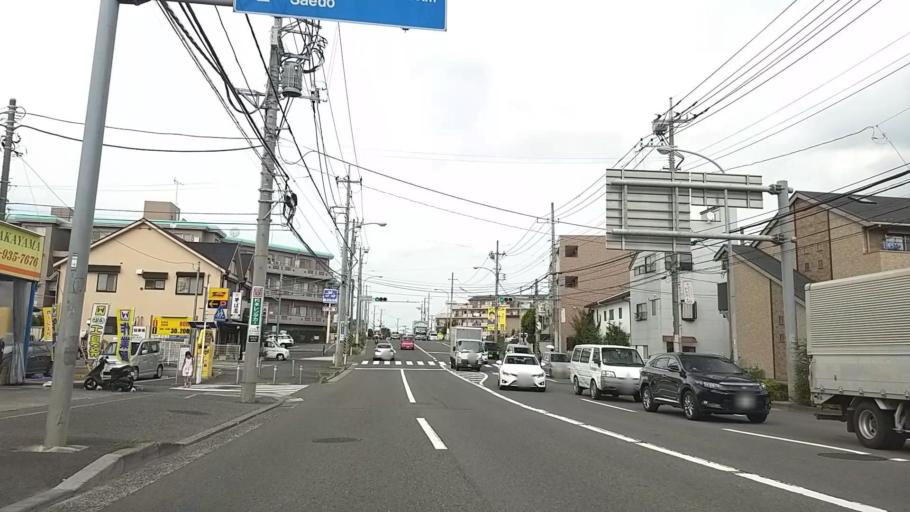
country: JP
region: Tokyo
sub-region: Machida-shi
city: Machida
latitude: 35.5109
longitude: 139.5458
